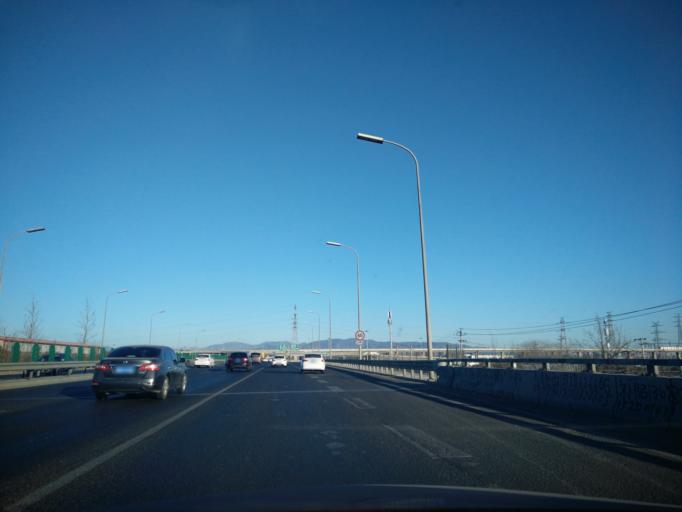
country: CN
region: Beijing
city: Lugu
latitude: 39.8594
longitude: 116.2119
